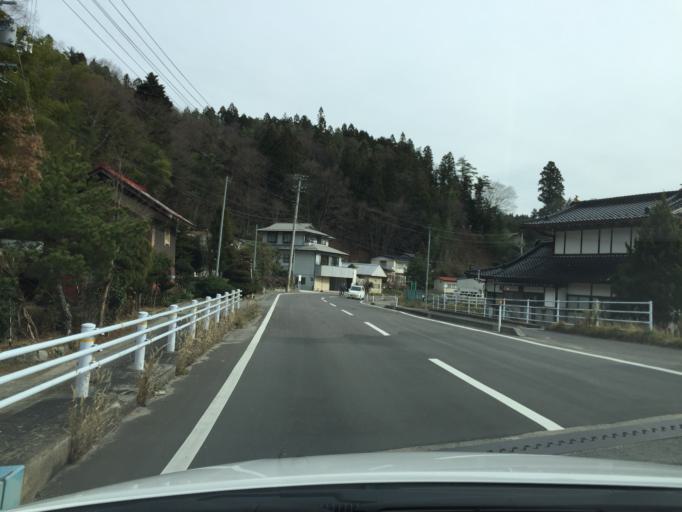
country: JP
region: Fukushima
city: Ishikawa
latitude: 37.2185
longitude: 140.5688
